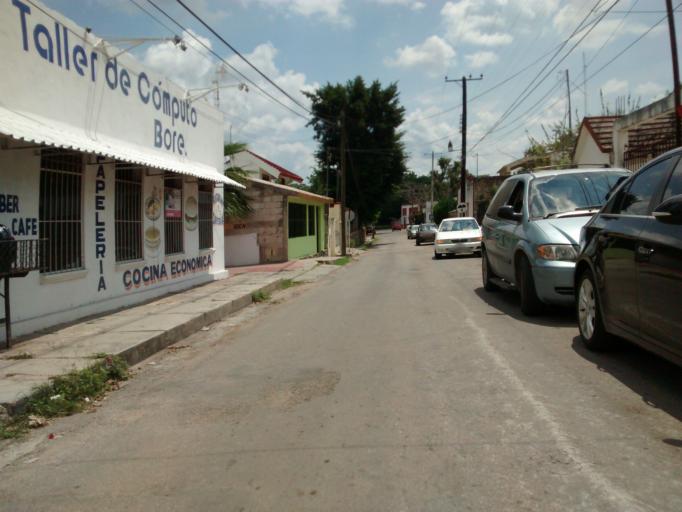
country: MX
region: Yucatan
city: Valladolid
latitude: 20.6856
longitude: -88.2120
